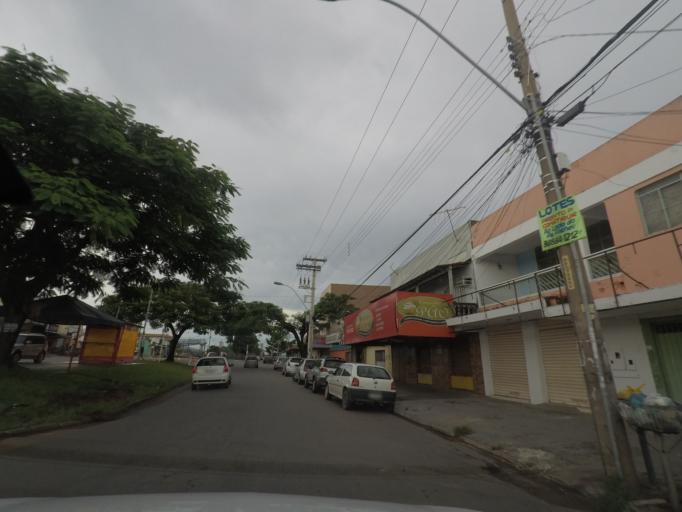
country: BR
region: Goias
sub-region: Goiania
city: Goiania
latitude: -16.7229
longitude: -49.2415
